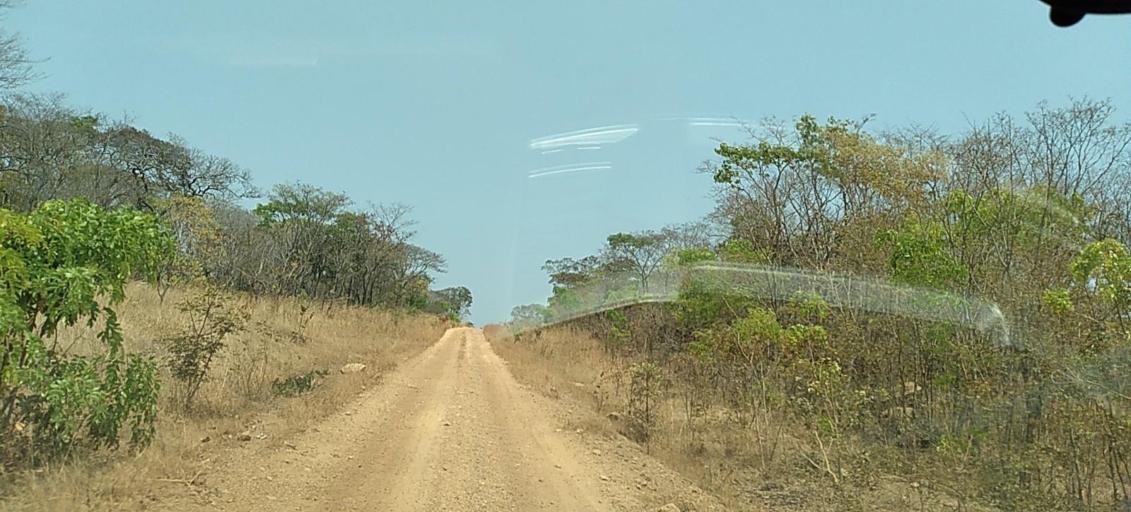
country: ZM
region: Central
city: Mumbwa
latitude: -14.4170
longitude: 26.4890
